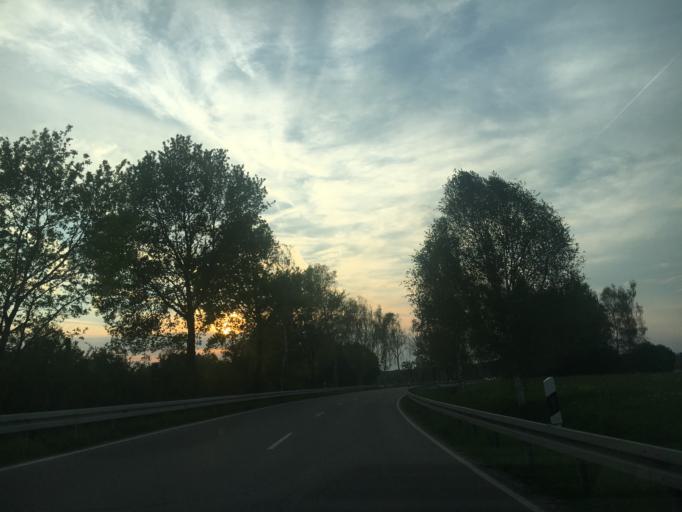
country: DE
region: Bavaria
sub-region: Upper Bavaria
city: Bichl
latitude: 47.7184
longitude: 11.4022
